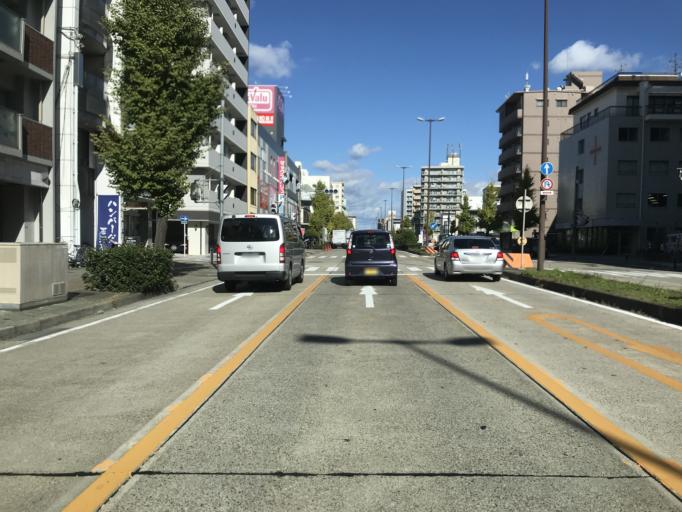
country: JP
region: Aichi
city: Nagoya-shi
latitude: 35.1724
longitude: 136.9379
